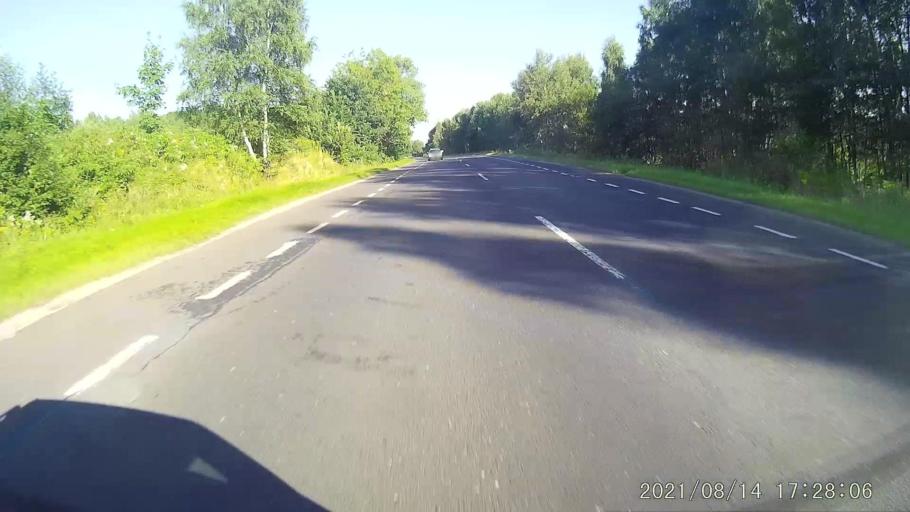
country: PL
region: Lower Silesian Voivodeship
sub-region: Jelenia Gora
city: Jelenia Gora
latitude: 50.9125
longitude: 15.6905
